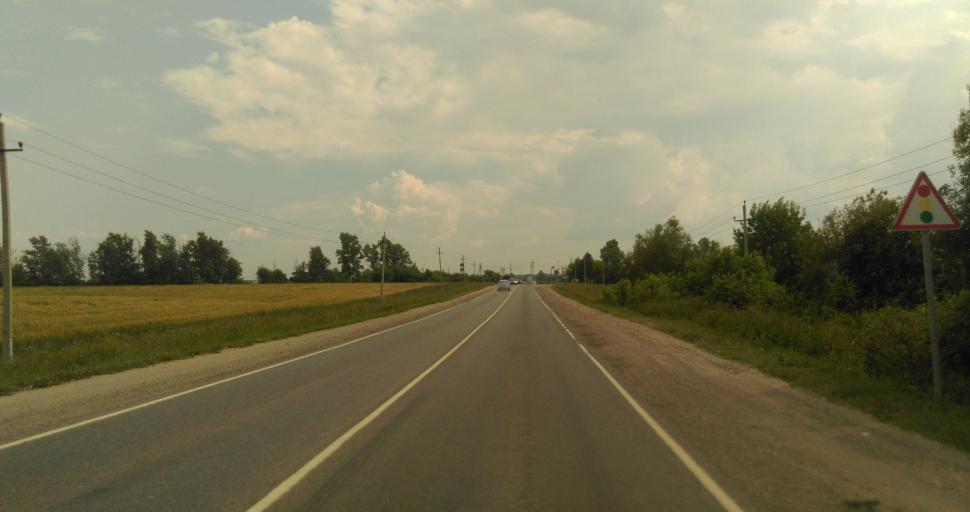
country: RU
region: Moskovskaya
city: Zhitnevo
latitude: 55.3574
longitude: 37.9075
